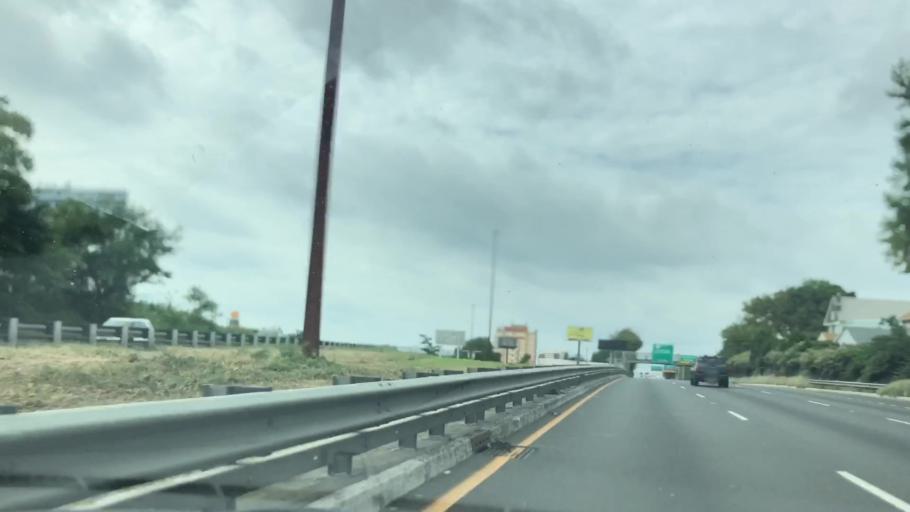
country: US
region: New Jersey
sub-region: Hudson County
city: Secaucus
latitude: 40.7952
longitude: -74.0597
